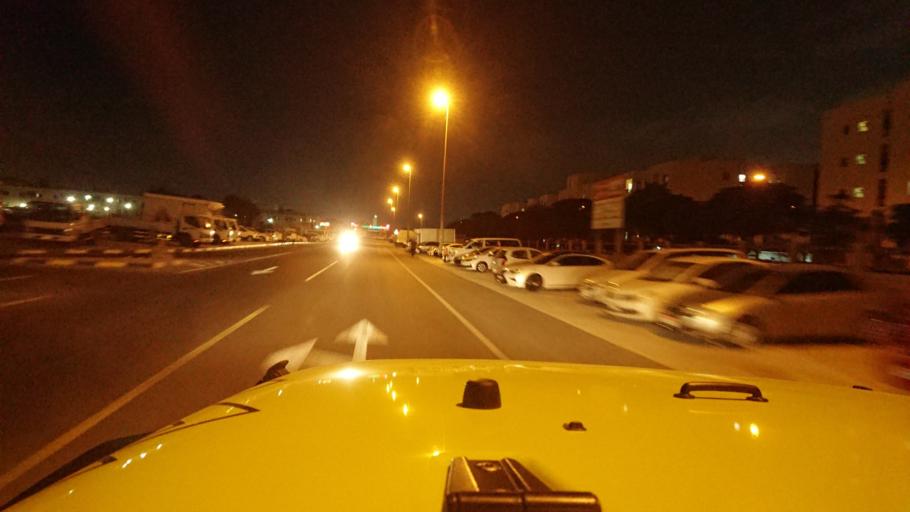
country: AE
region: Dubai
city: Dubai
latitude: 25.1416
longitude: 55.2563
